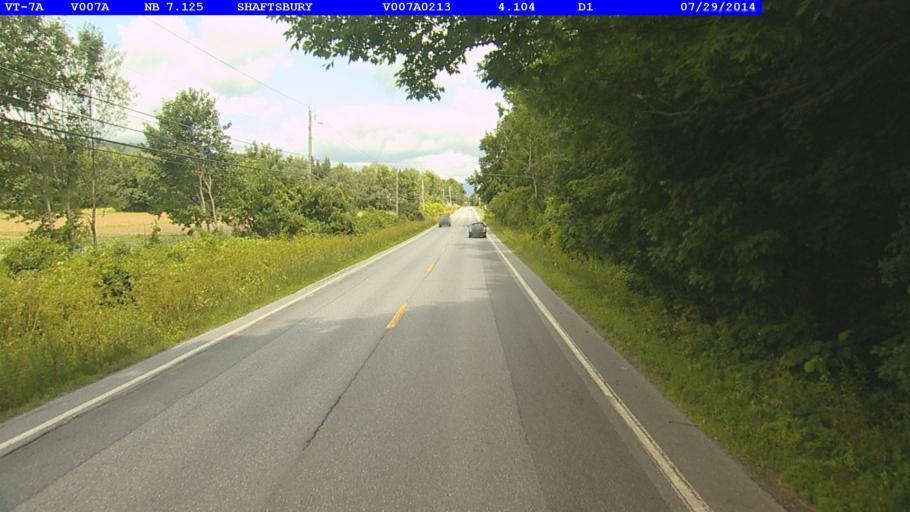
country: US
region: Vermont
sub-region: Bennington County
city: North Bennington
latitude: 42.9911
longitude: -73.2048
